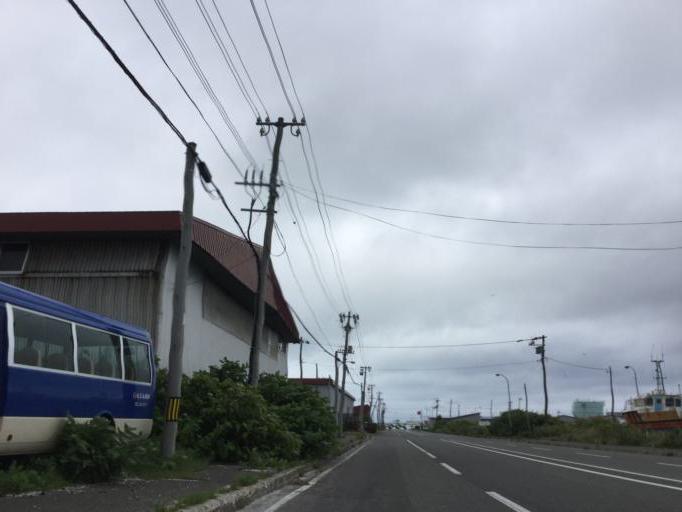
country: JP
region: Hokkaido
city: Wakkanai
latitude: 45.4057
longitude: 141.6822
